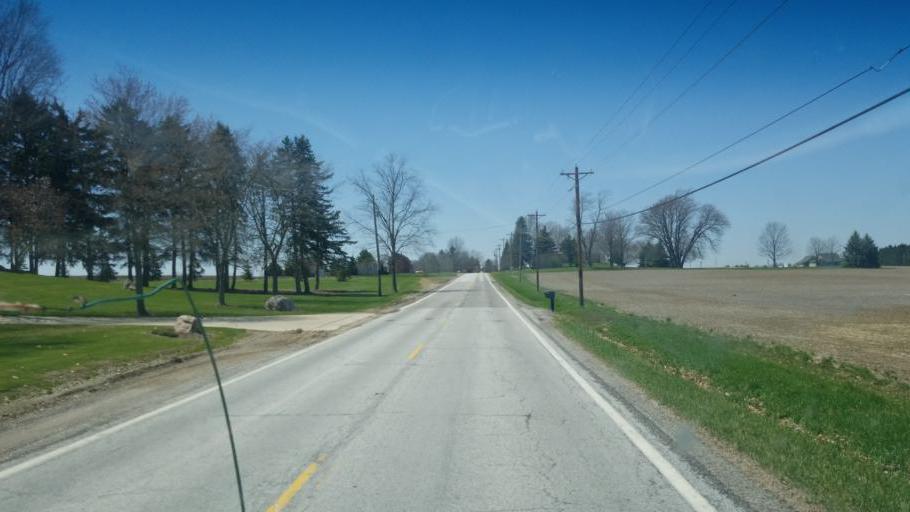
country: US
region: Ohio
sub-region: Huron County
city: New London
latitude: 41.0897
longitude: -82.4565
